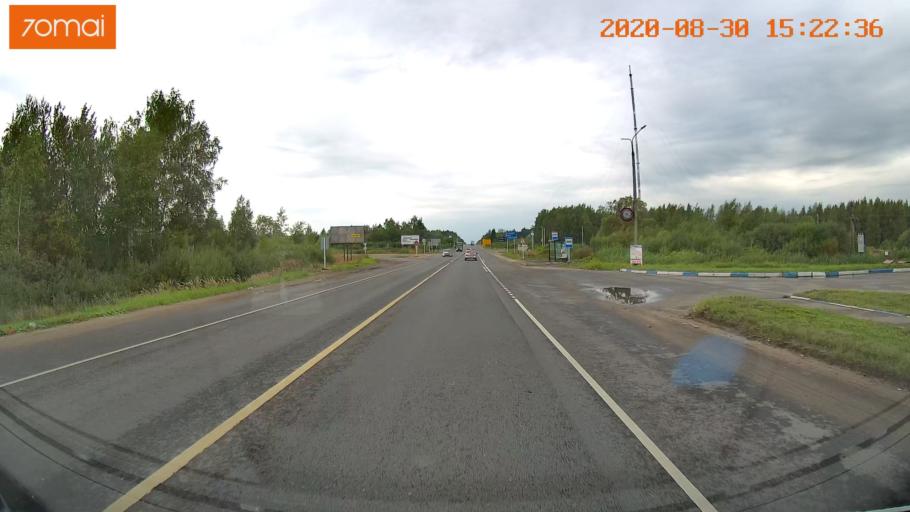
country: RU
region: Ivanovo
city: Rodniki
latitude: 57.0880
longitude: 41.7245
